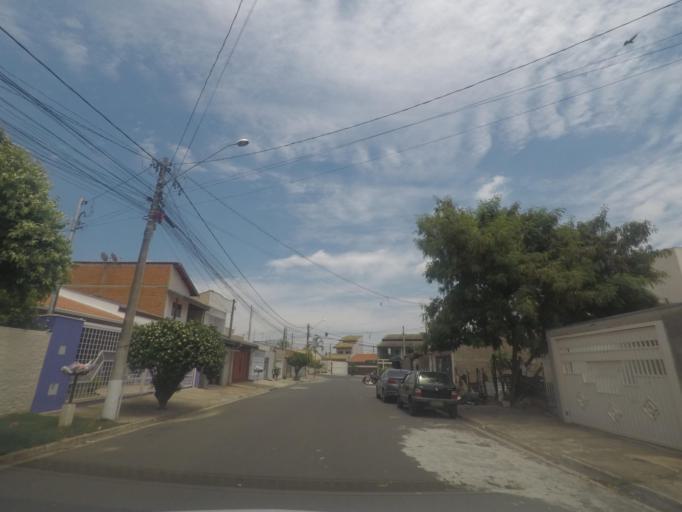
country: BR
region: Sao Paulo
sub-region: Sumare
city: Sumare
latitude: -22.8007
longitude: -47.2738
